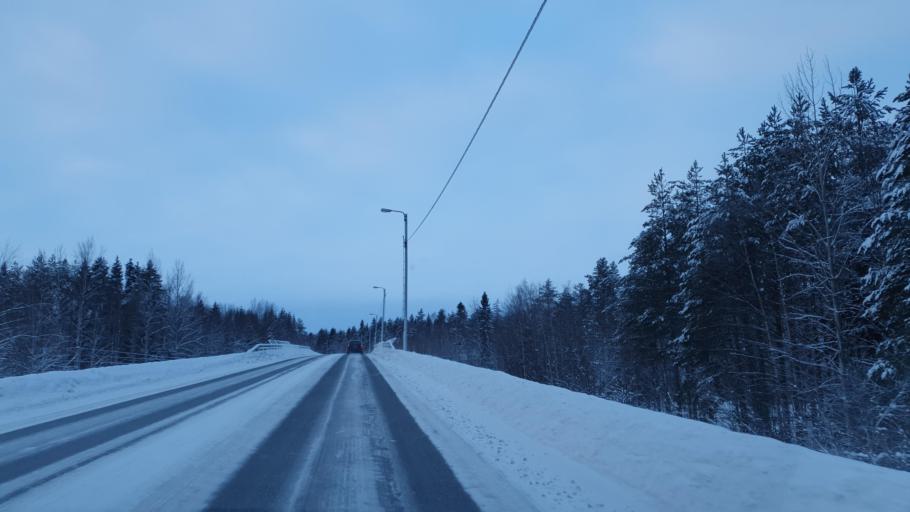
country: FI
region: Northern Ostrobothnia
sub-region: Oulu
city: Haukipudas
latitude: 65.2007
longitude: 25.4082
